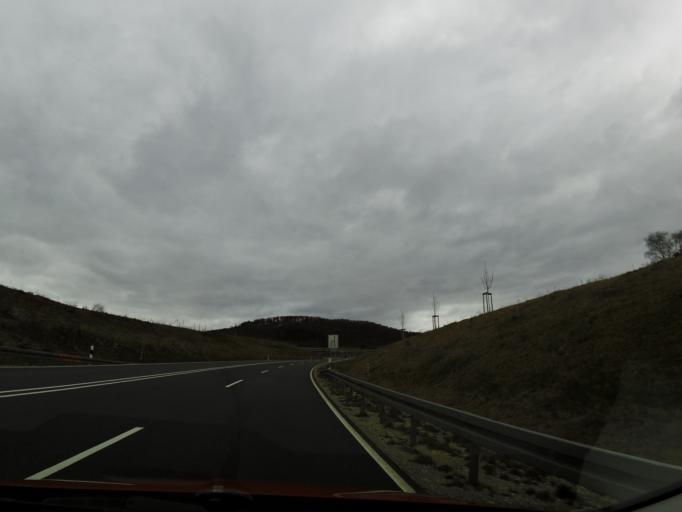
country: DE
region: Lower Saxony
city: Waake
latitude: 51.5596
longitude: 10.0617
